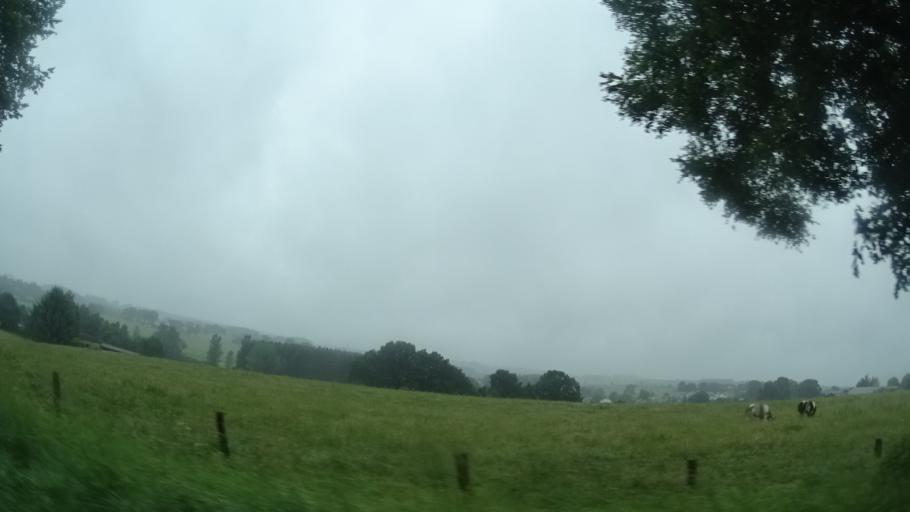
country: BE
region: Wallonia
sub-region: Province du Luxembourg
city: Bertrix
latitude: 49.8415
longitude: 5.3393
